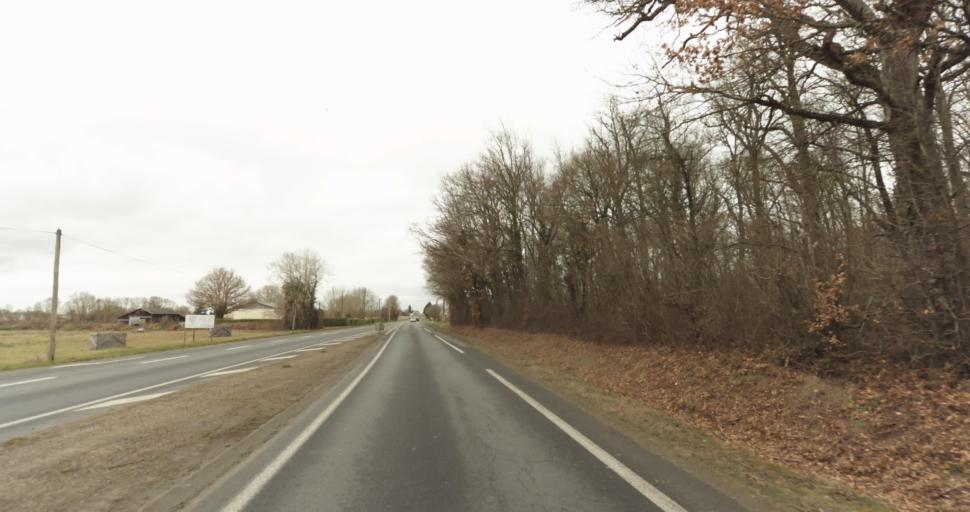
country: FR
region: Pays de la Loire
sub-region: Departement de Maine-et-Loire
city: Vivy
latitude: 47.3385
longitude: -0.0679
